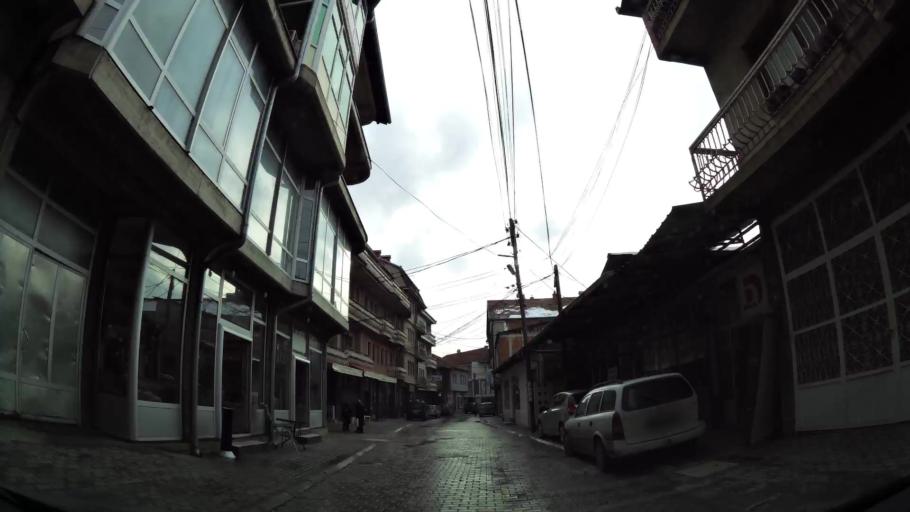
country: XK
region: Pristina
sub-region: Komuna e Prishtines
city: Pristina
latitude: 42.6721
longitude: 21.1656
